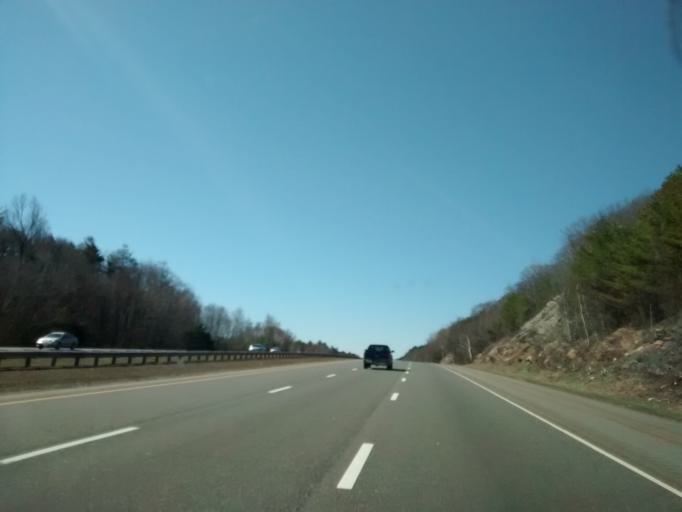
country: US
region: Massachusetts
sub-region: Hampden County
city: Holland
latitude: 42.0104
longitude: -72.1594
